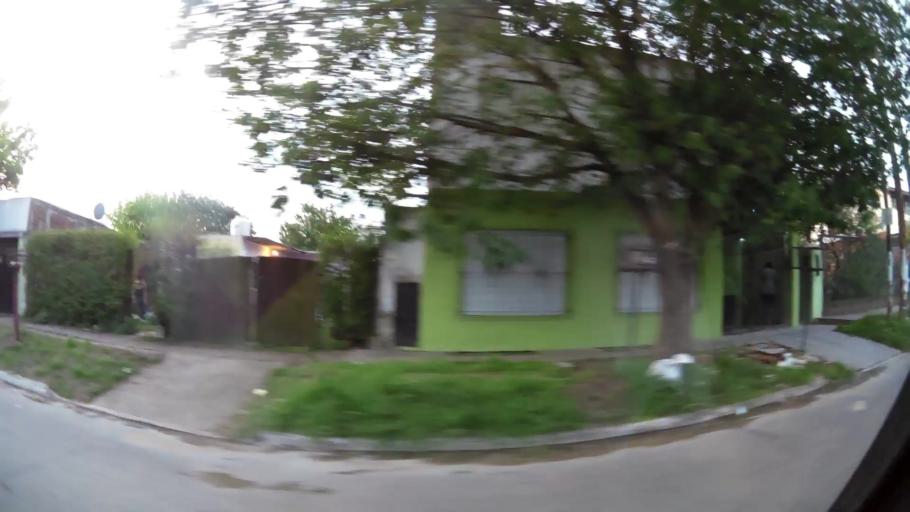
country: AR
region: Buenos Aires
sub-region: Partido de Quilmes
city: Quilmes
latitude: -34.7977
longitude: -58.2857
